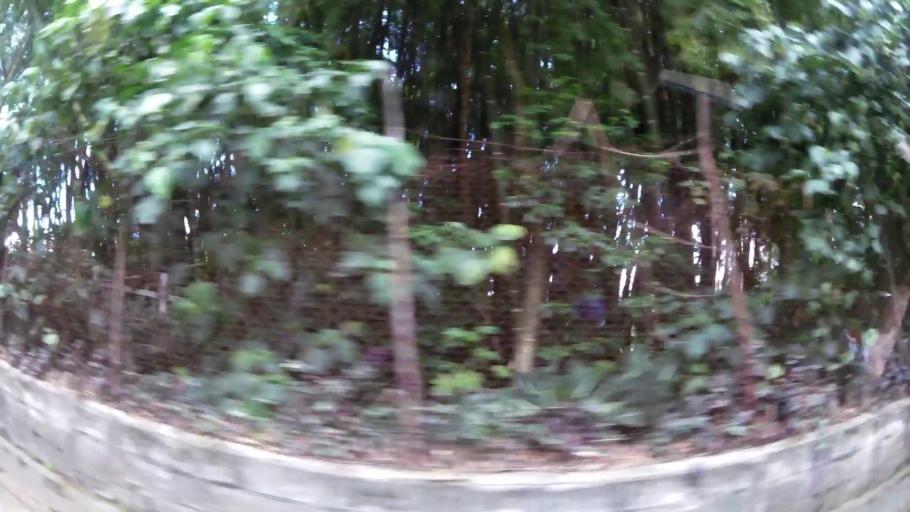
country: CO
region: Antioquia
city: La Estrella
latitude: 6.1644
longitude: -75.6418
